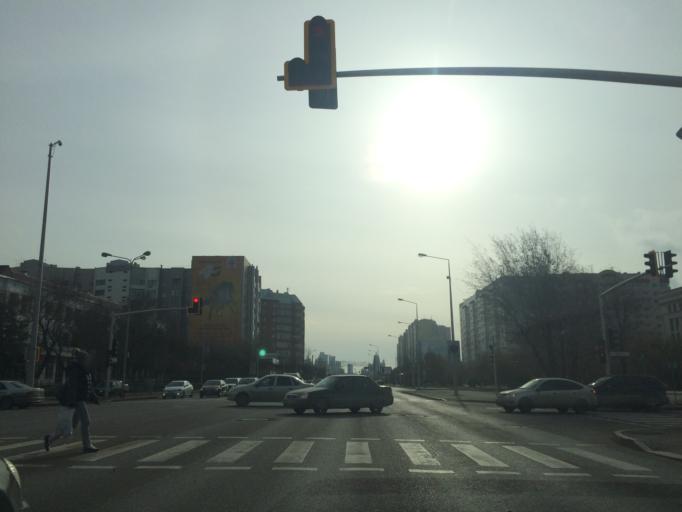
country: KZ
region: Astana Qalasy
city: Astana
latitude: 51.1664
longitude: 71.4087
